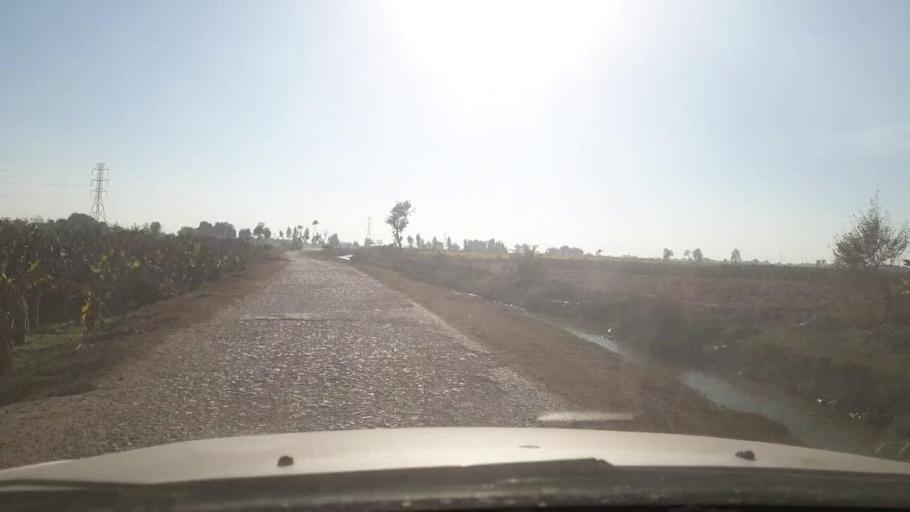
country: PK
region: Sindh
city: Adilpur
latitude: 27.9563
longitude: 69.2210
